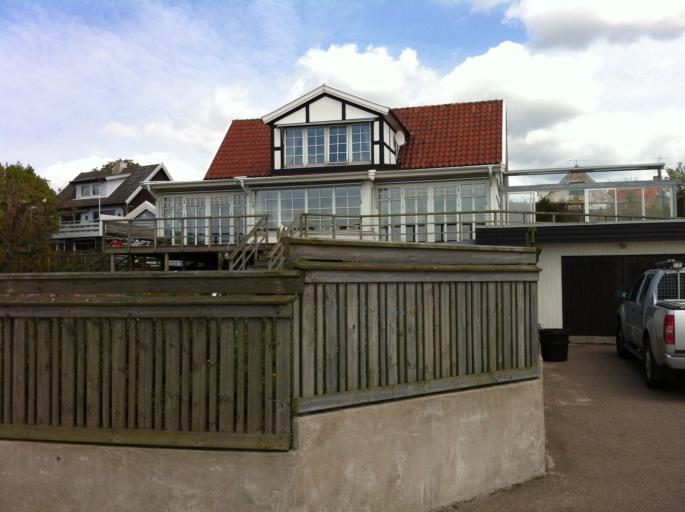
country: SE
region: Skane
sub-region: Hoganas Kommun
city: Hoganas
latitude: 56.1413
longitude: 12.5838
